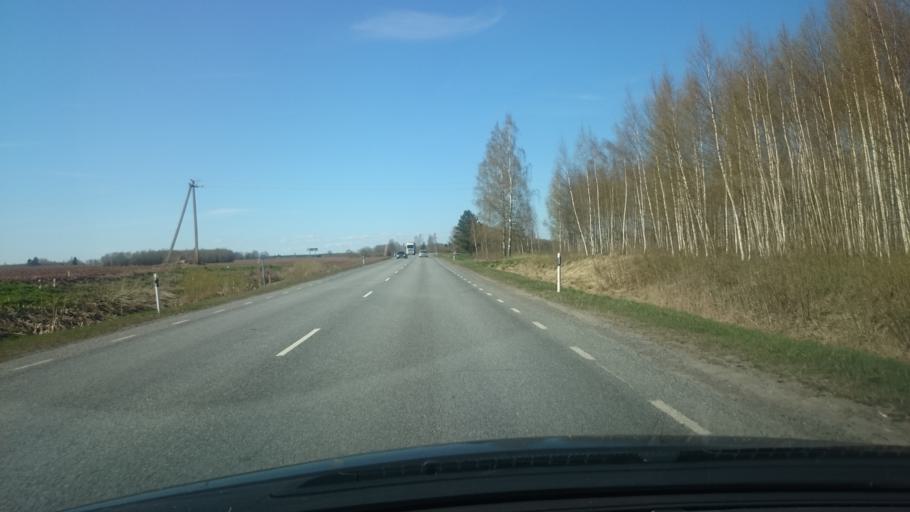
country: EE
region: Polvamaa
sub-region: Polva linn
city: Polva
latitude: 58.2685
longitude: 27.0045
